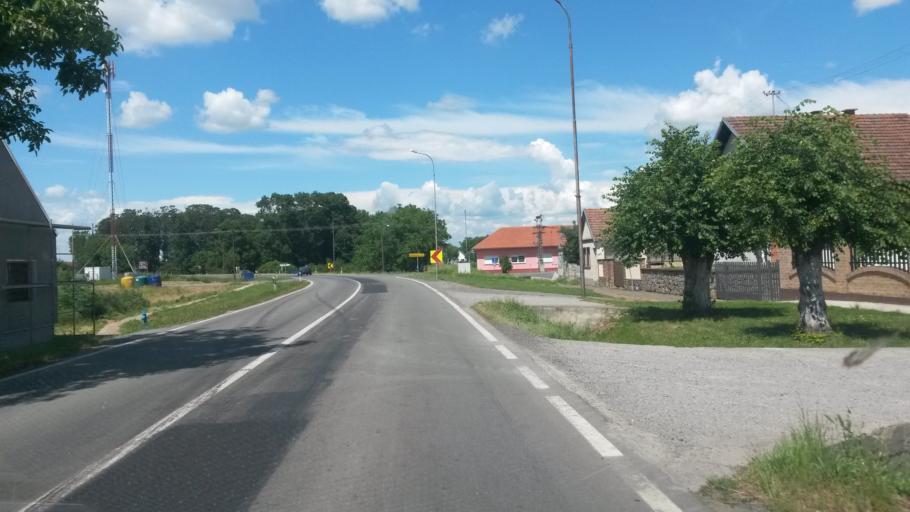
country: HR
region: Osjecko-Baranjska
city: Vuka
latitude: 45.4398
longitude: 18.5074
